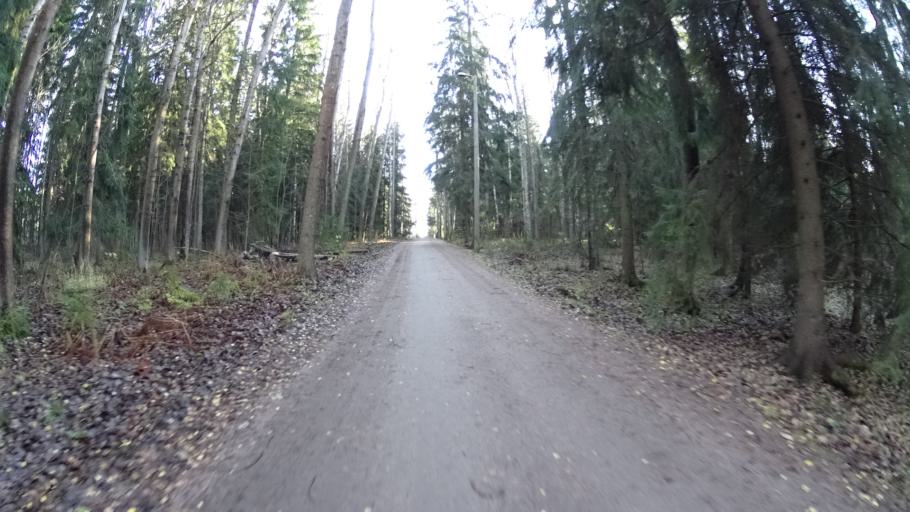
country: FI
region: Uusimaa
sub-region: Helsinki
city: Helsinki
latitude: 60.2218
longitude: 24.9188
